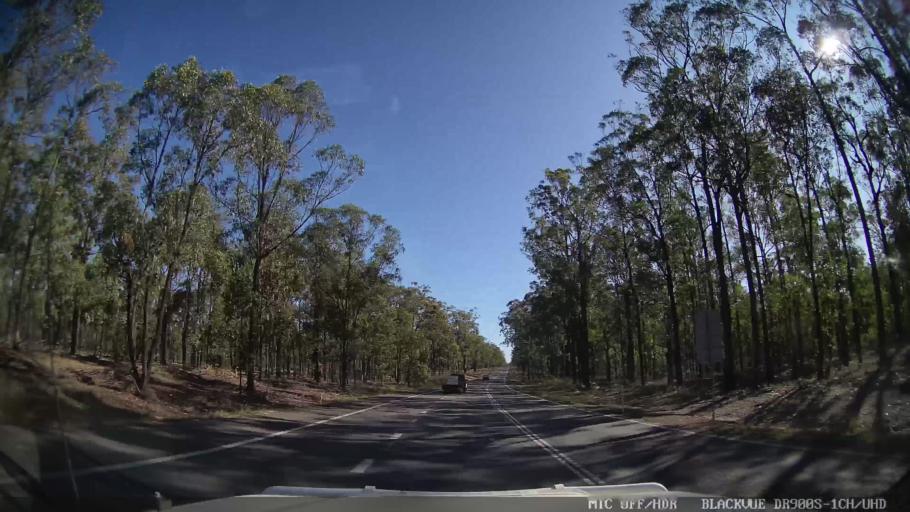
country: AU
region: Queensland
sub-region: Bundaberg
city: Childers
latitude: -25.2156
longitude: 152.0775
